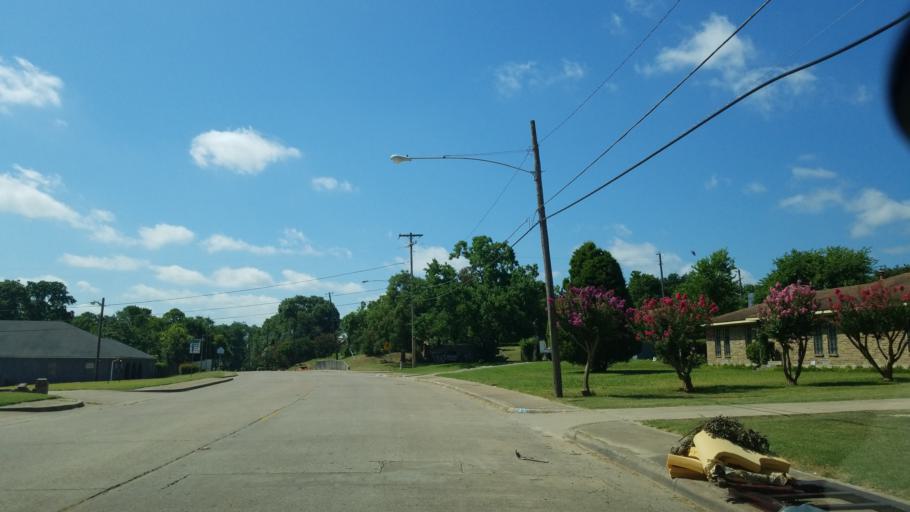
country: US
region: Texas
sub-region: Dallas County
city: Dallas
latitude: 32.7297
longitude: -96.7924
